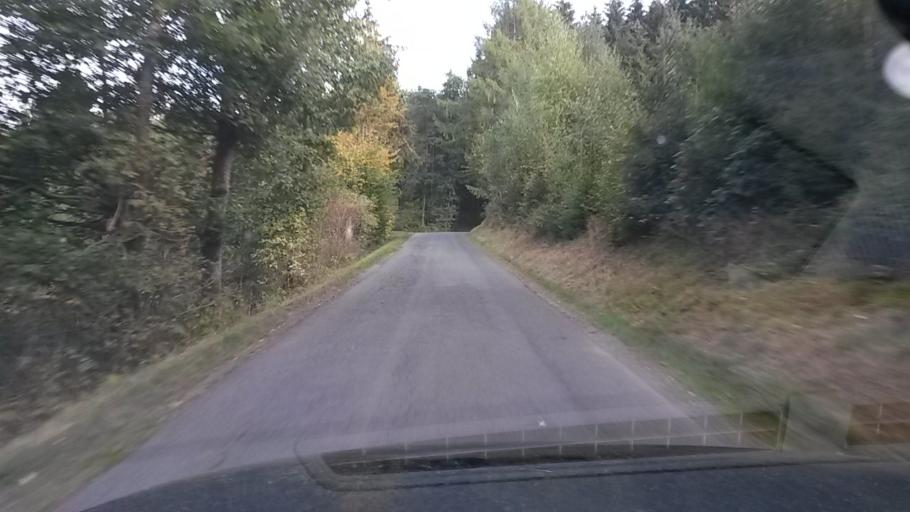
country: DE
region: North Rhine-Westphalia
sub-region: Regierungsbezirk Arnsberg
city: Herscheid
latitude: 51.2151
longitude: 7.7488
